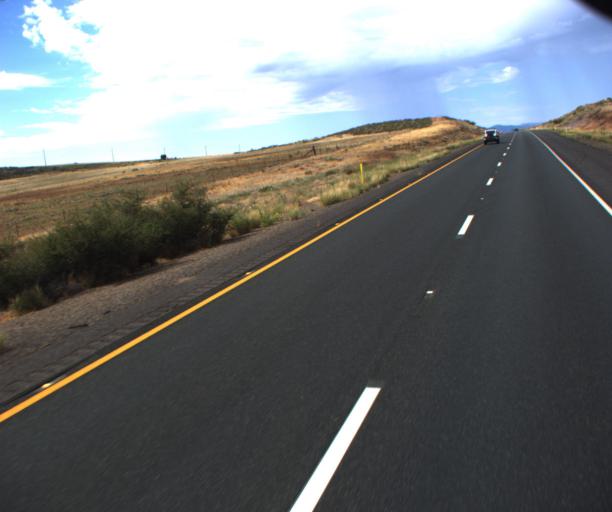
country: US
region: Arizona
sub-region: Yavapai County
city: Cordes Lakes
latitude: 34.4421
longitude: -112.0398
